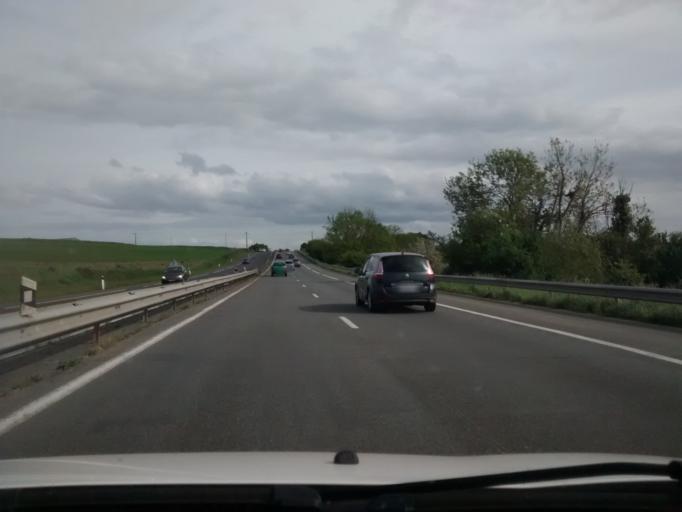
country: FR
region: Brittany
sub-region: Departement d'Ille-et-Vilaine
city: Saint-Jouan-des-Guerets
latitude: 48.5908
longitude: -1.9584
